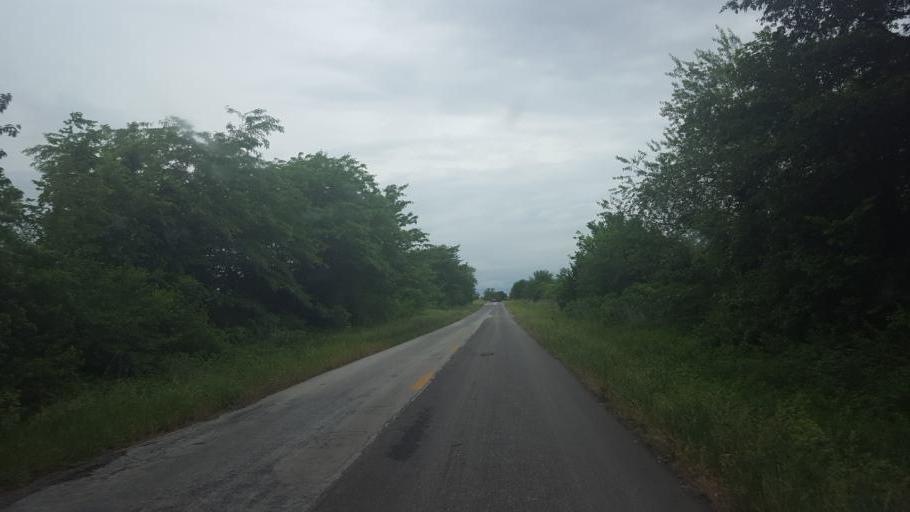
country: US
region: Missouri
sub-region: Moniteau County
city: California
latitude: 38.8072
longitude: -92.6047
